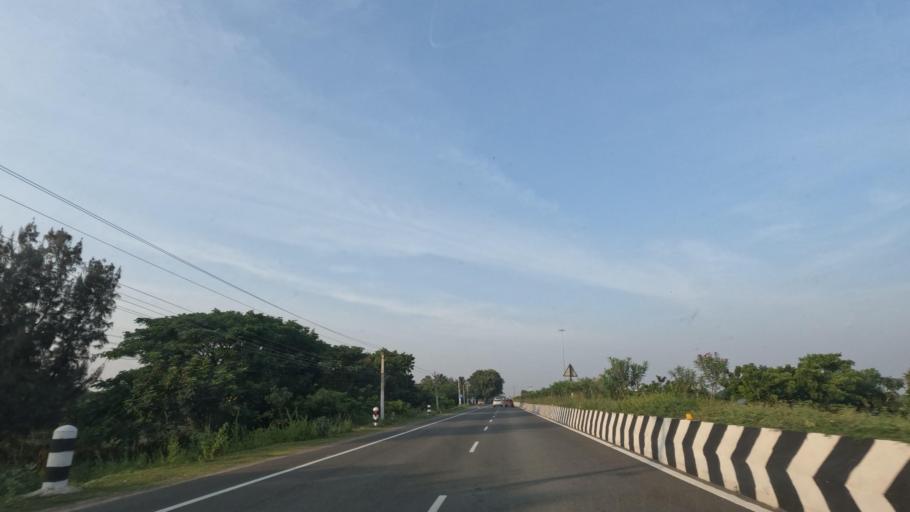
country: IN
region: Tamil Nadu
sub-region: Kancheepuram
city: Mamallapuram
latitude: 12.6873
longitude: 80.2164
